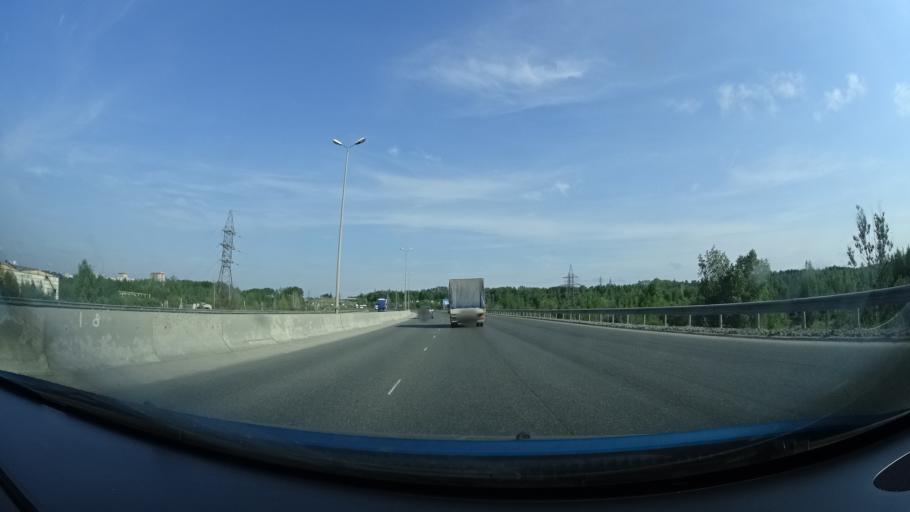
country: RU
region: Perm
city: Kondratovo
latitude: 58.0347
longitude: 56.0549
